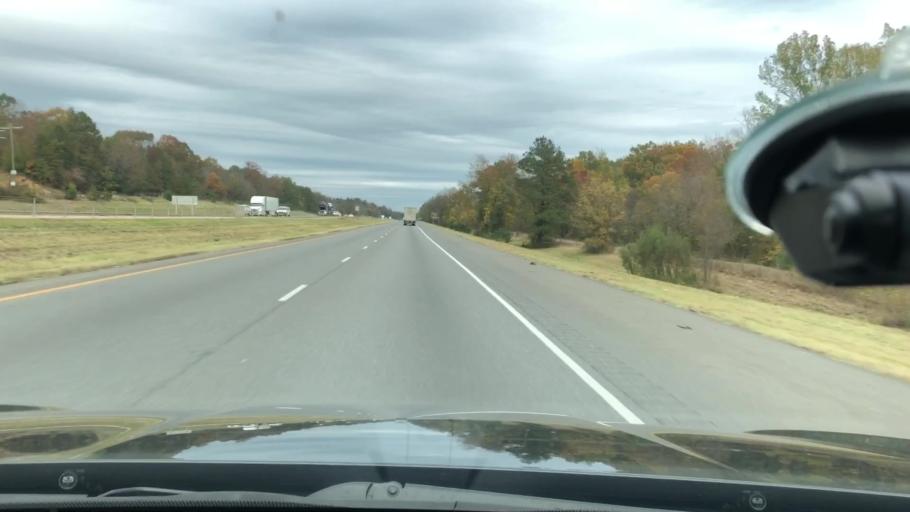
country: US
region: Arkansas
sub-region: Hot Spring County
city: Malvern
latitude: 34.3744
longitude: -92.8560
